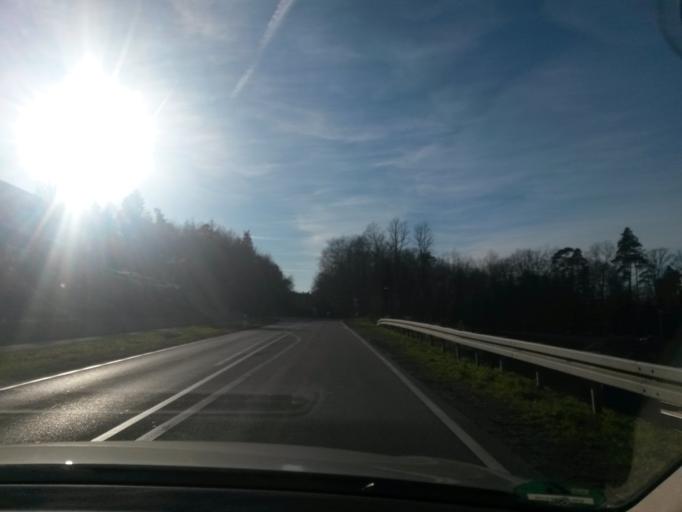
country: DE
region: Baden-Wuerttemberg
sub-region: Karlsruhe Region
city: Neuenburg
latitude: 48.8513
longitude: 8.5775
